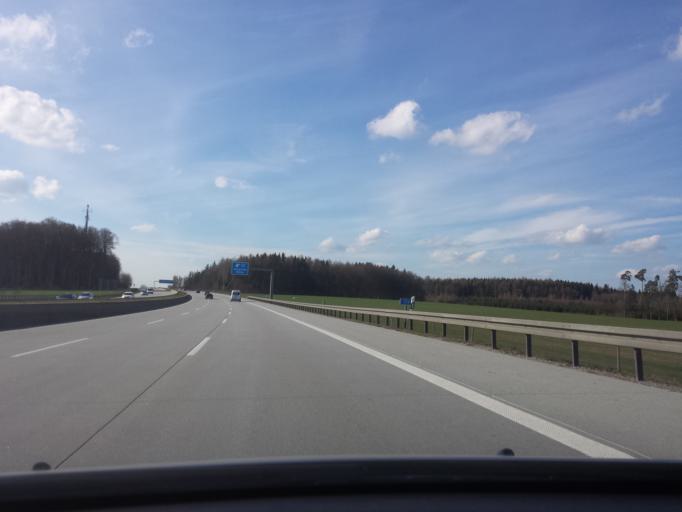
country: DE
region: Bavaria
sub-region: Upper Bavaria
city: Sulzemoos
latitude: 48.2743
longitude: 11.2832
